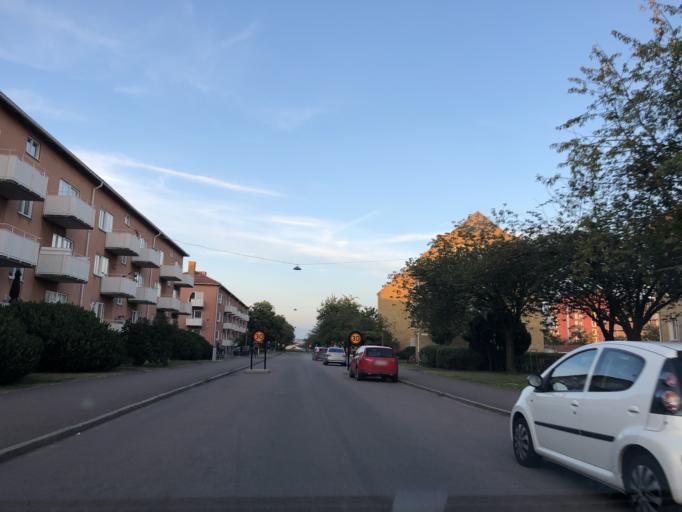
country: SE
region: Vaestra Goetaland
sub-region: Goteborg
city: Majorna
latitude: 57.7287
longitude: 11.9295
